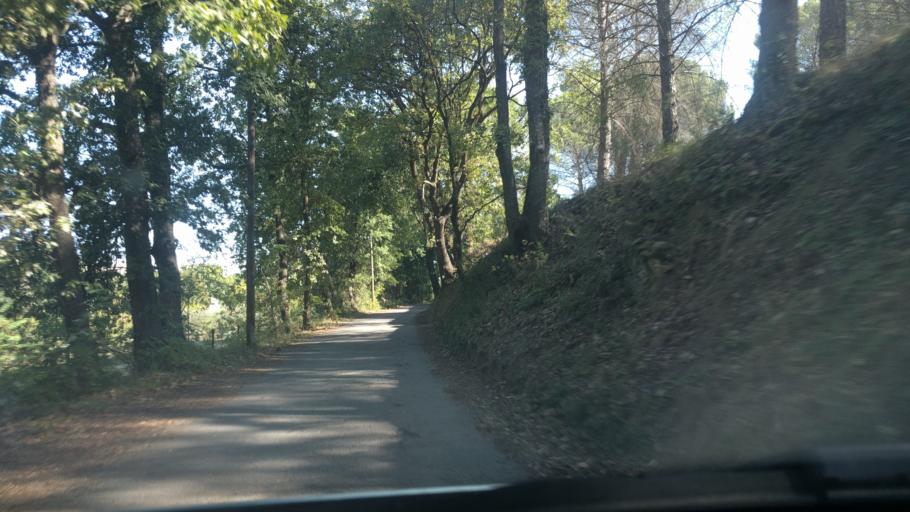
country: FR
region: Provence-Alpes-Cote d'Azur
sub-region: Departement du Vaucluse
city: Pertuis
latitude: 43.7195
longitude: 5.5470
